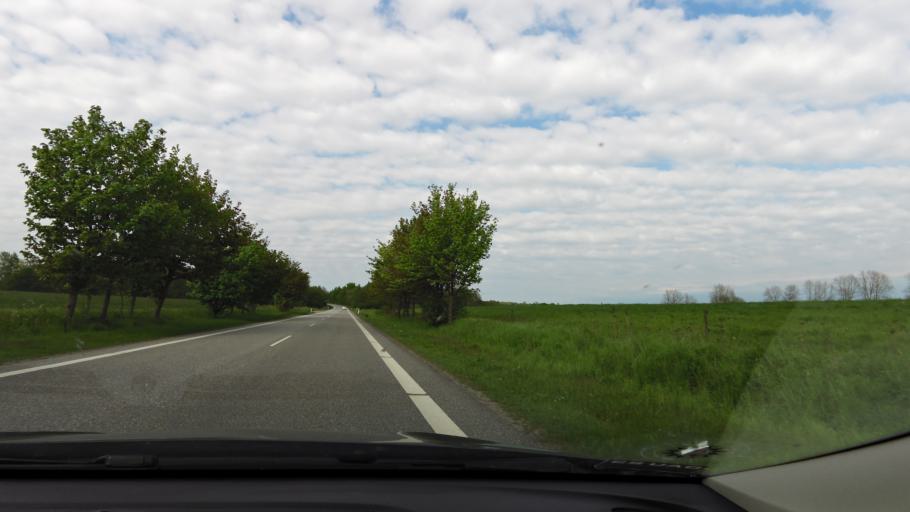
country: DK
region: South Denmark
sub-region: Nyborg Kommune
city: Nyborg
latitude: 55.3257
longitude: 10.7375
